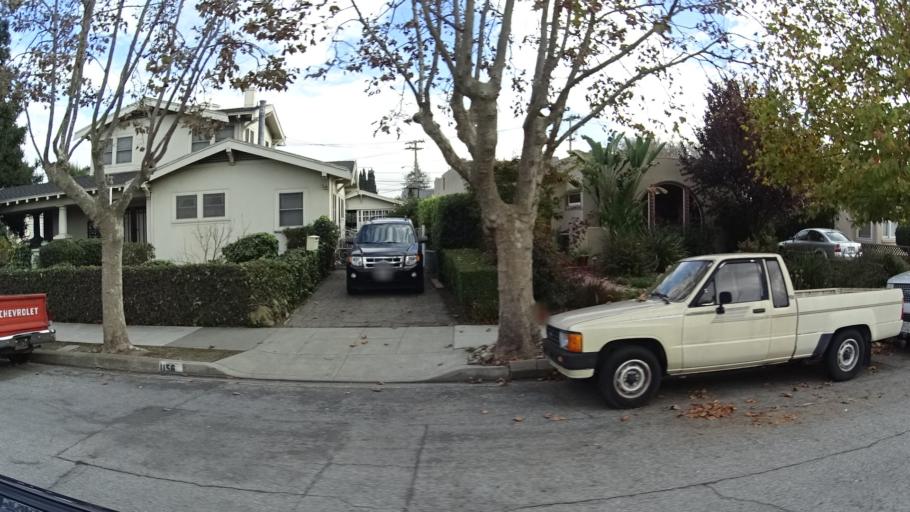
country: US
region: California
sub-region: Santa Clara County
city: Buena Vista
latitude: 37.3292
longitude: -121.9123
